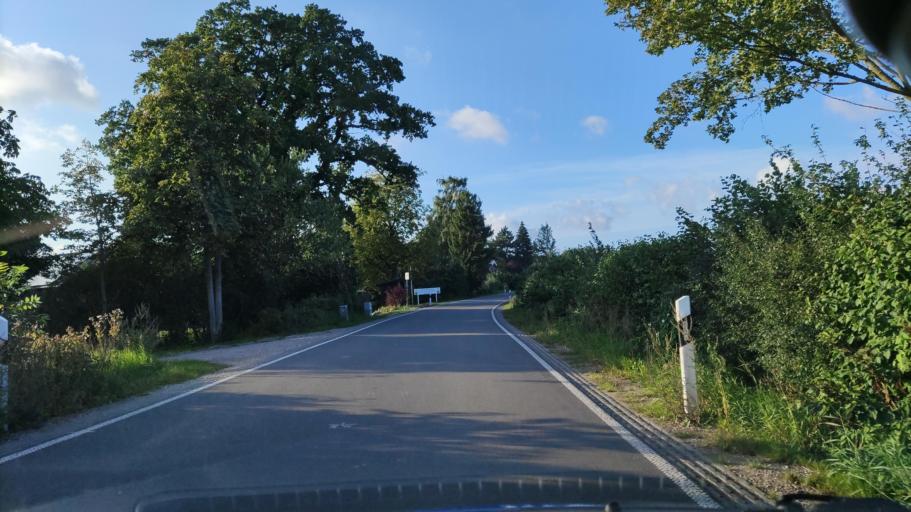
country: DE
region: Schleswig-Holstein
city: Bosau
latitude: 54.1003
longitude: 10.4803
